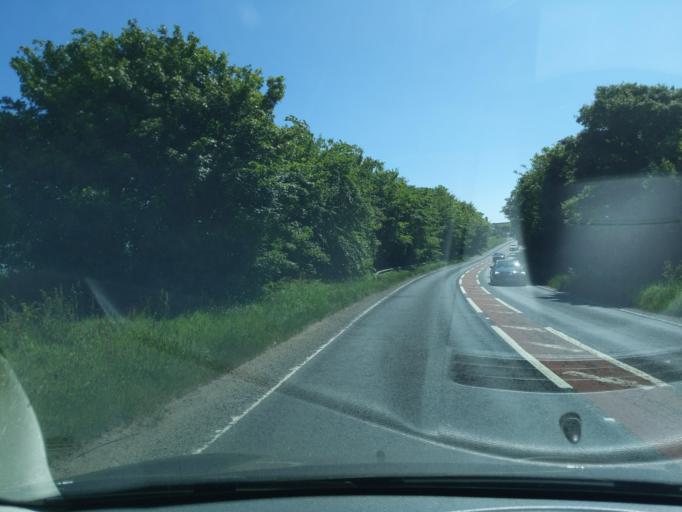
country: GB
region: England
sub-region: Cornwall
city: Wendron
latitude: 50.1270
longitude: -5.2303
